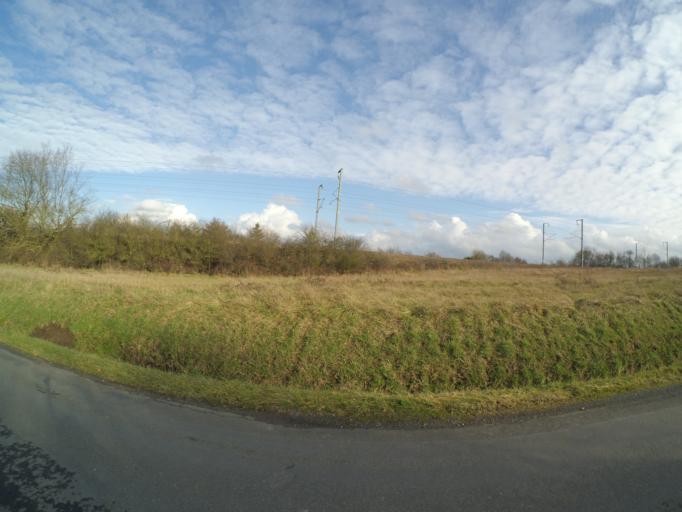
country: FR
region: Pays de la Loire
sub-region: Departement de la Loire-Atlantique
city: Clisson
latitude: 47.0780
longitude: -1.2773
